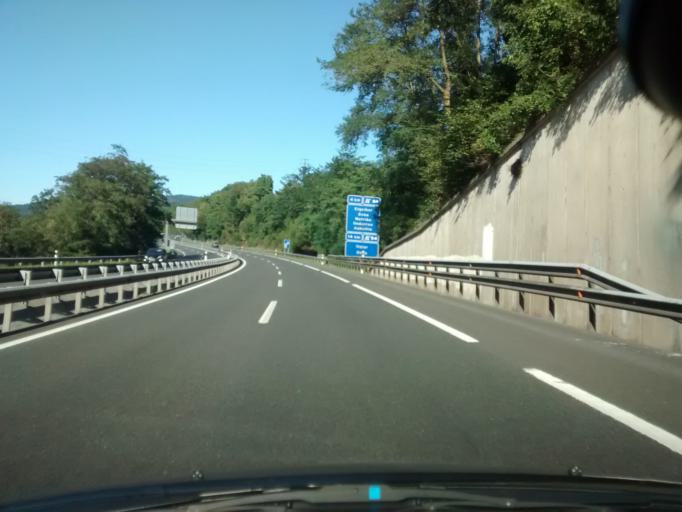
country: ES
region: Basque Country
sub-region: Provincia de Guipuzcoa
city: Elgoibar
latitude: 43.2042
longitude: -2.4234
